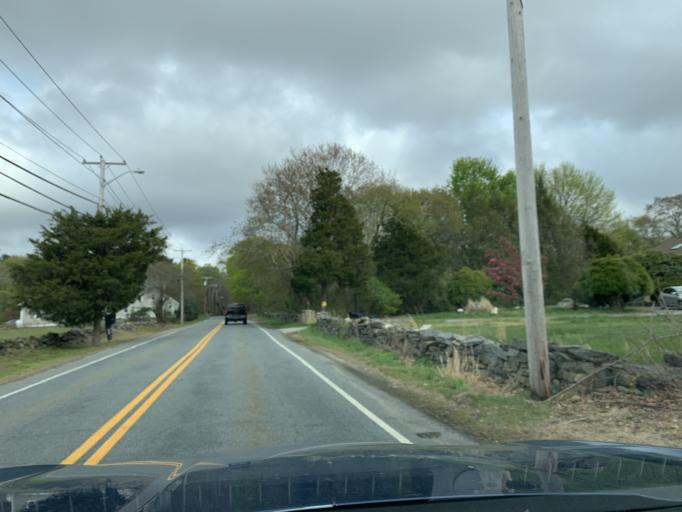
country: US
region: Rhode Island
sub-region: Washington County
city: North Kingstown
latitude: 41.5909
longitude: -71.4801
